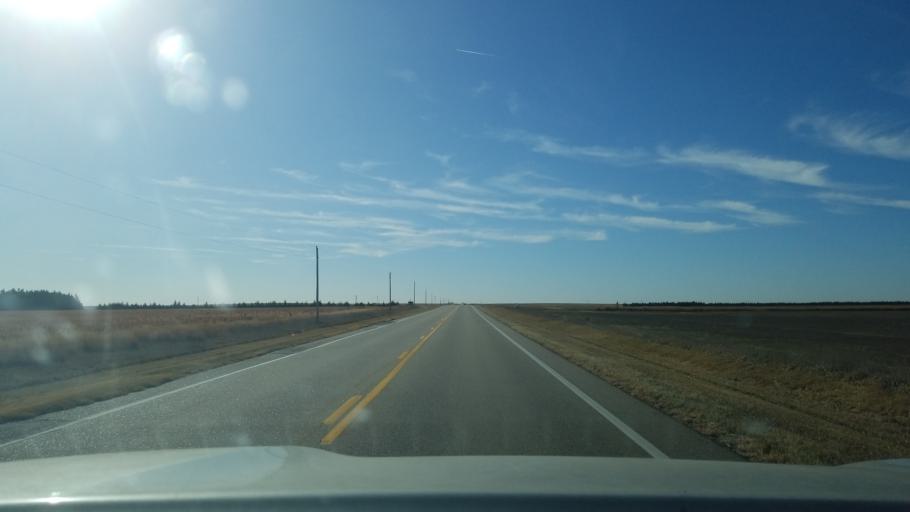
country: US
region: Kansas
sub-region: Ness County
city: Ness City
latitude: 38.3610
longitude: -99.8979
